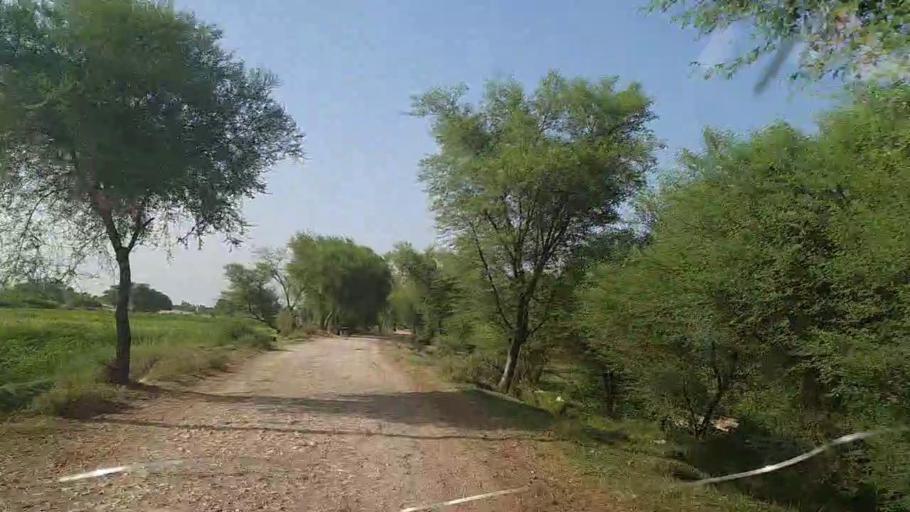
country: PK
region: Sindh
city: Khanpur
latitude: 27.7189
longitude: 69.3317
